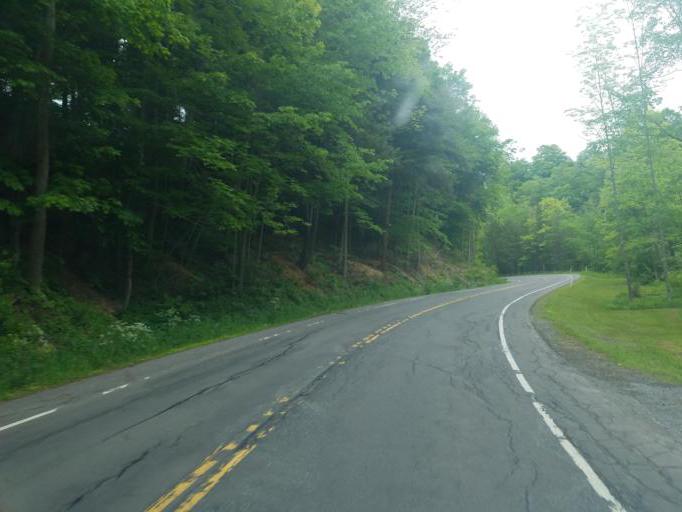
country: US
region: New York
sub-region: Herkimer County
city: Frankfort
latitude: 42.9426
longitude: -75.1141
